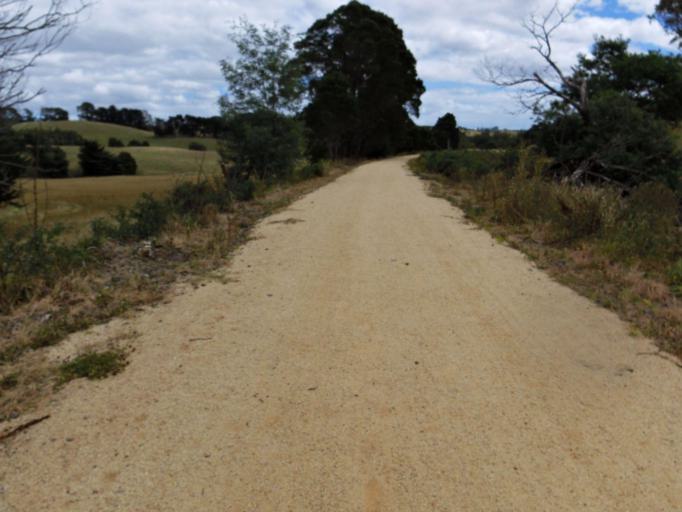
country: AU
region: Victoria
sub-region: Bass Coast
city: North Wonthaggi
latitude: -38.4178
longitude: 145.7480
